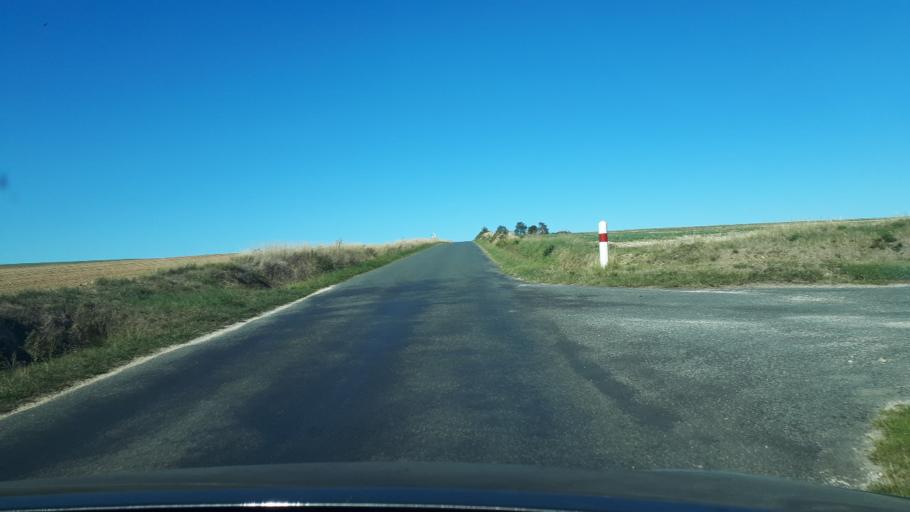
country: FR
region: Centre
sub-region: Departement du Cher
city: Baugy
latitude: 47.2106
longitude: 2.7441
